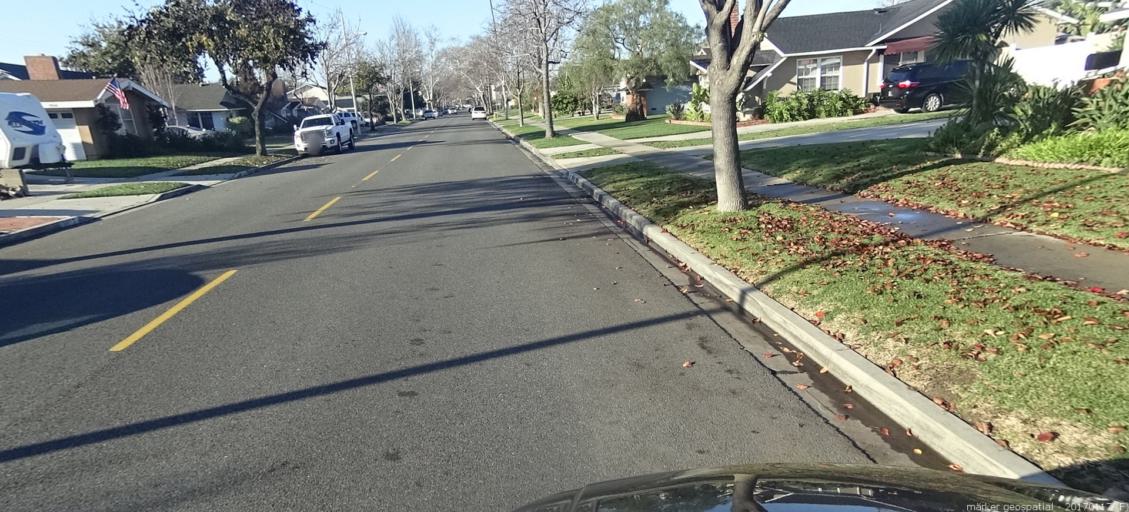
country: US
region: California
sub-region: Orange County
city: Rossmoor
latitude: 33.7786
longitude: -118.0800
